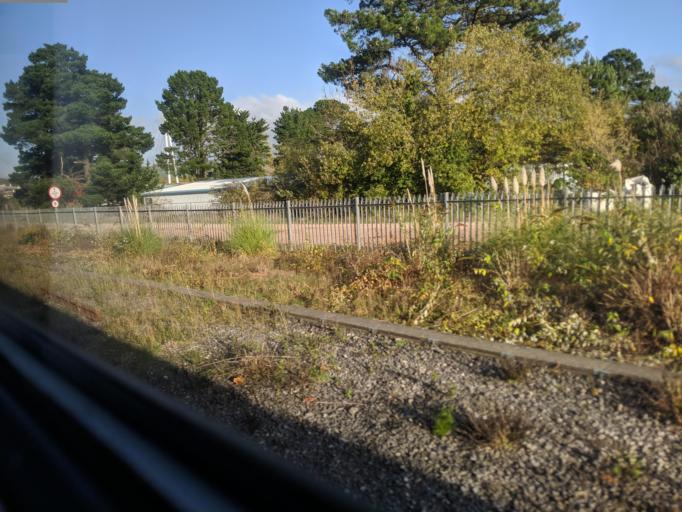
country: GB
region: England
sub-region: Devon
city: Newton Abbot
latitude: 50.5324
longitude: -3.5986
